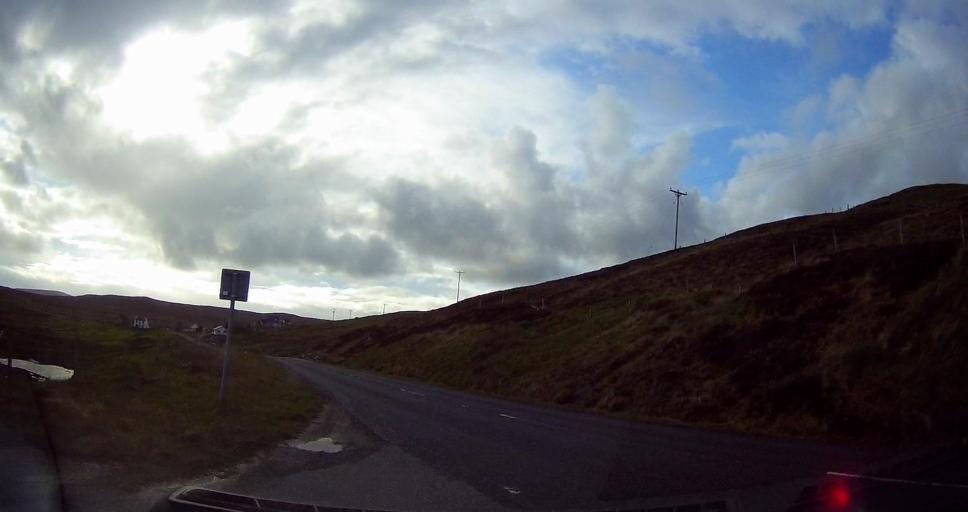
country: GB
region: Scotland
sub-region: Shetland Islands
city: Lerwick
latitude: 60.3532
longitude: -1.1877
